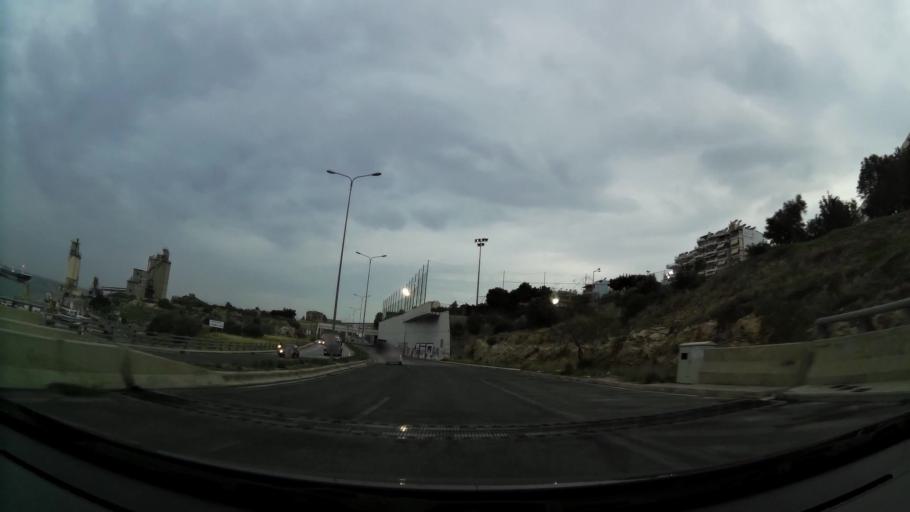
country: GR
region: Attica
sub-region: Nomos Piraios
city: Drapetsona
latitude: 37.9493
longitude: 23.6164
